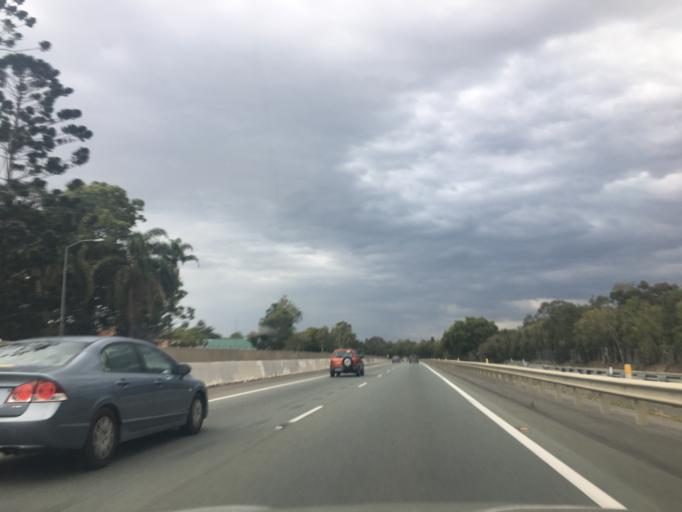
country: AU
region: Queensland
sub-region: Brisbane
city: Bald Hills
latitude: -27.3103
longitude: 153.0120
